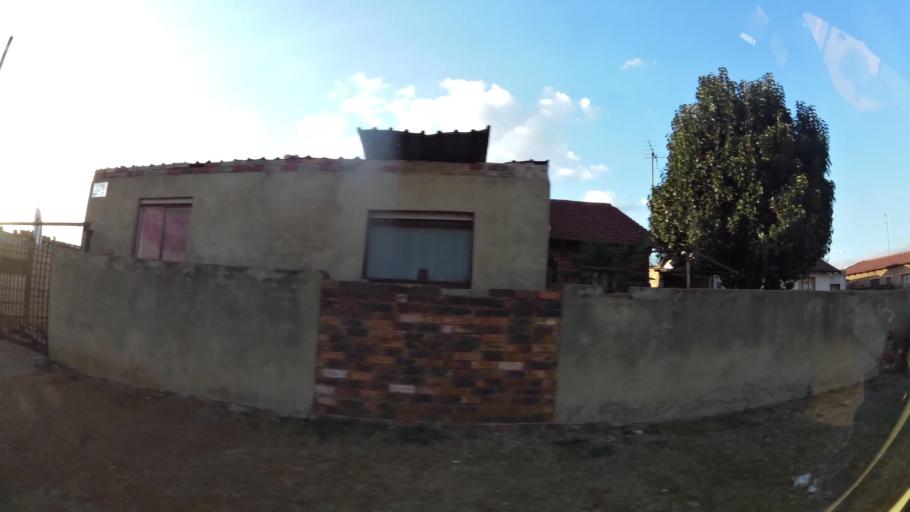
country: ZA
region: Gauteng
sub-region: West Rand District Municipality
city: Krugersdorp
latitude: -26.0749
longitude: 27.7573
